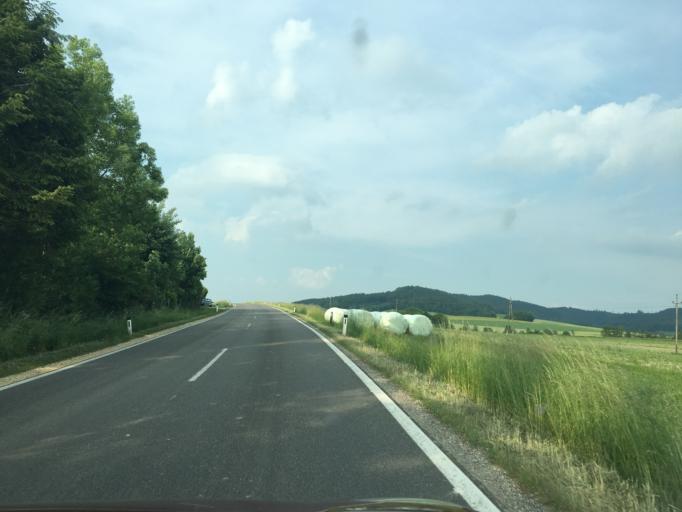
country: AT
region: Upper Austria
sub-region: Politischer Bezirk Ried im Innkreis
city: Ried im Innkreis
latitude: 48.1610
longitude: 13.5683
